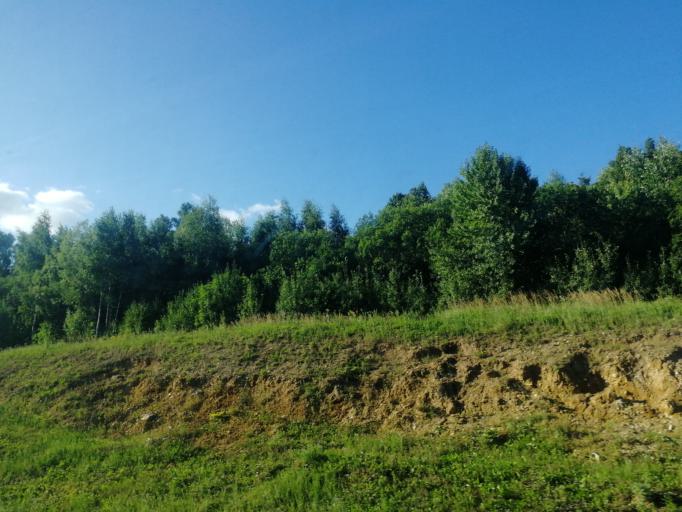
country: RU
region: Tula
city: Novogurovskiy
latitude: 54.2781
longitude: 37.2445
